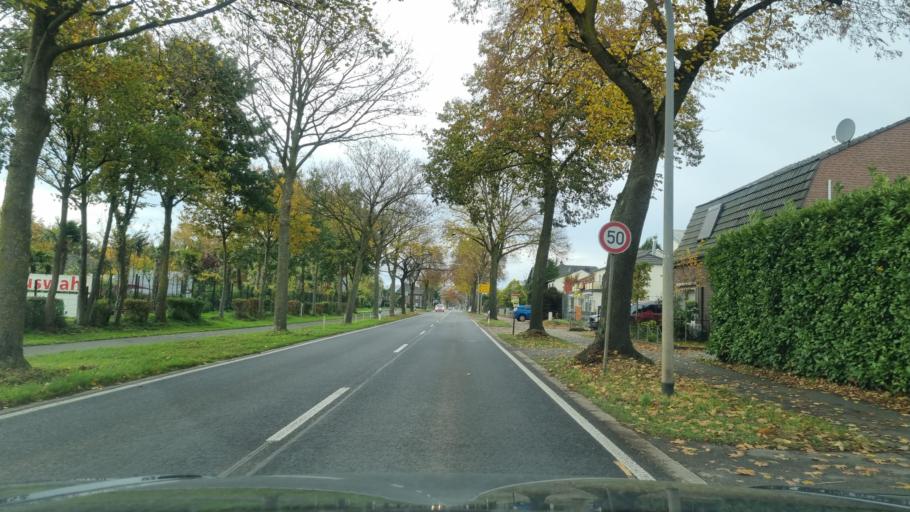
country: DE
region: North Rhine-Westphalia
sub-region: Regierungsbezirk Dusseldorf
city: Kleve
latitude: 51.7676
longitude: 6.1370
